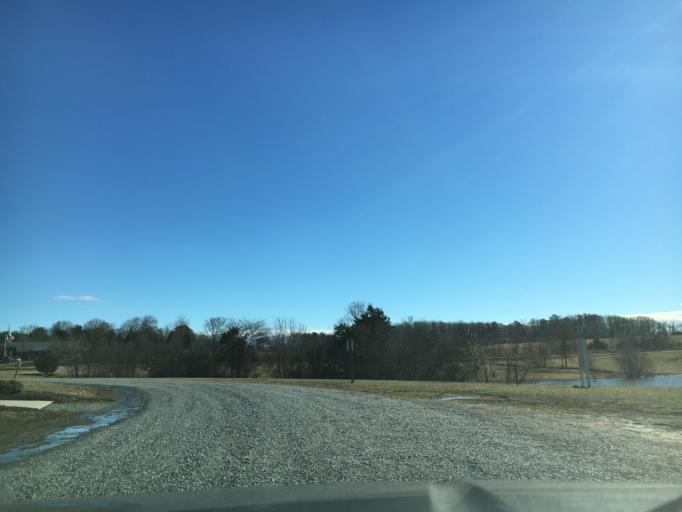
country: US
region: Virginia
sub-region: Halifax County
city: South Boston
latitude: 36.7205
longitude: -78.8671
